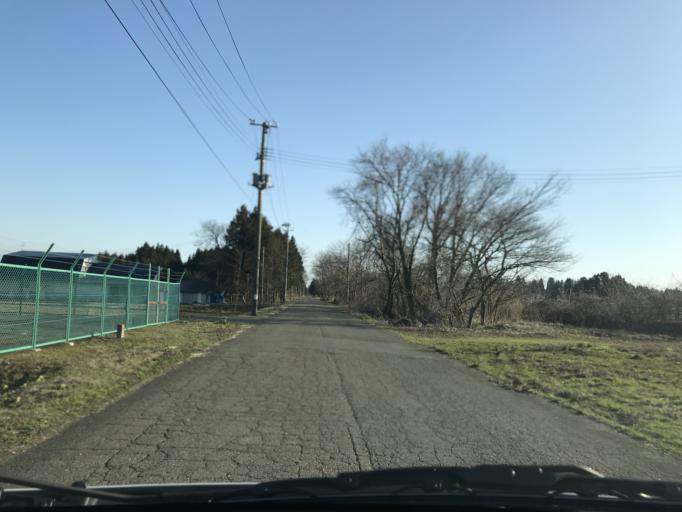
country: JP
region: Iwate
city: Kitakami
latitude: 39.2505
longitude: 141.0400
